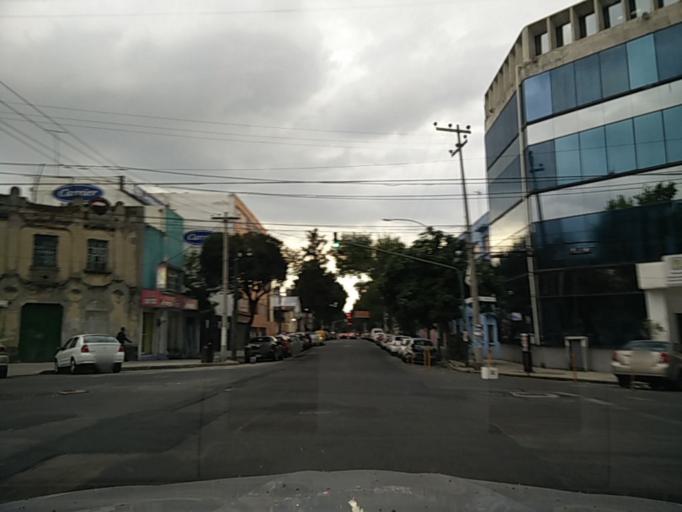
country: MX
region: Mexico City
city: Mexico City
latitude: 19.4191
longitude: -99.1457
